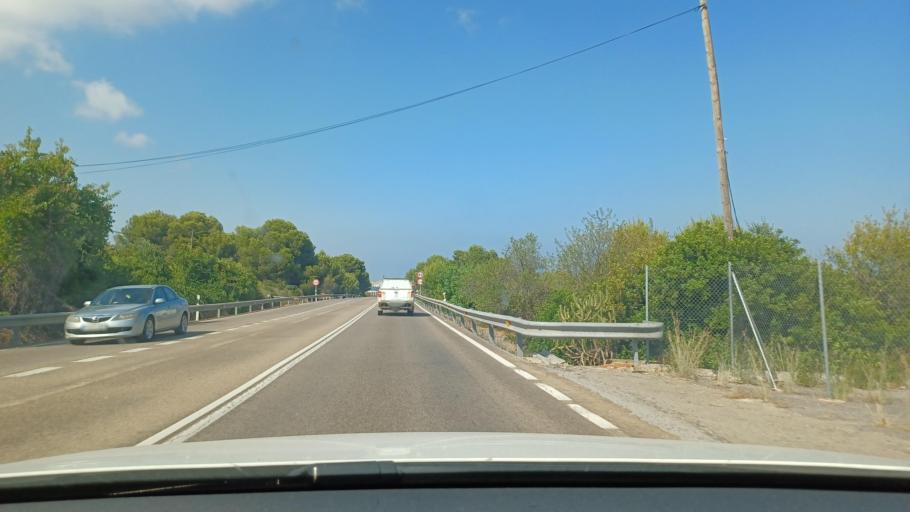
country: ES
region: Valencia
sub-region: Provincia de Castello
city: Orpesa/Oropesa del Mar
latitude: 40.0842
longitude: 0.1209
